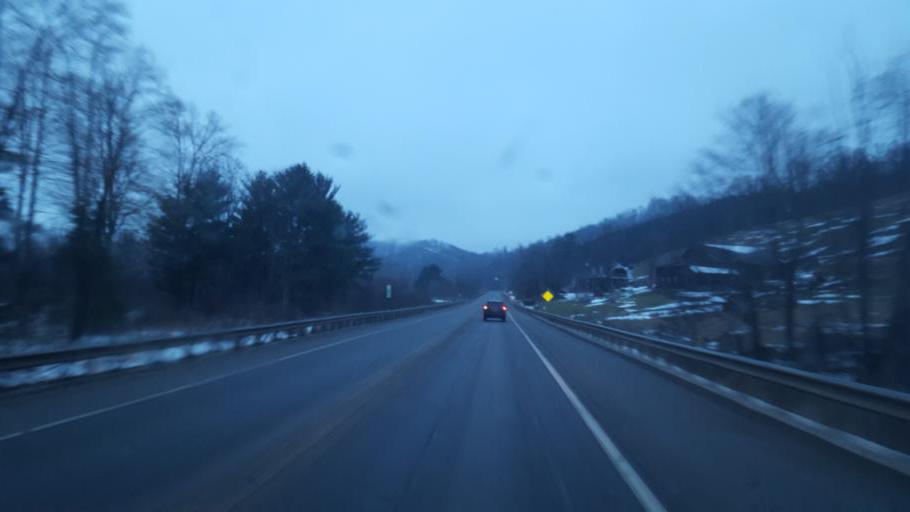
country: US
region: Pennsylvania
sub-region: McKean County
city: Port Allegany
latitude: 41.7901
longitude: -78.1761
